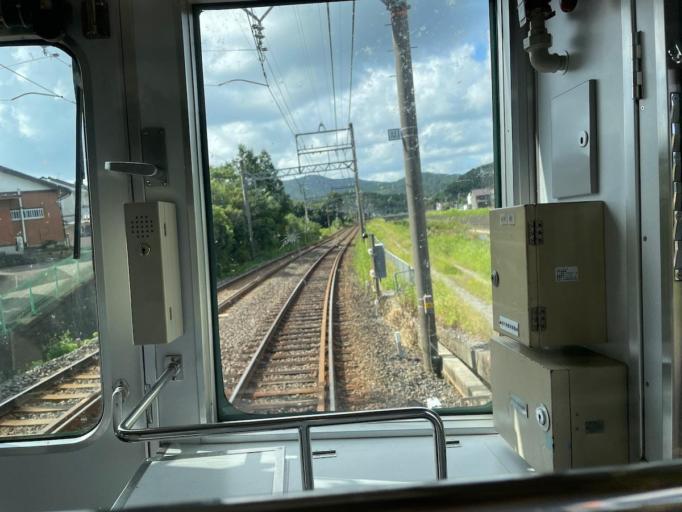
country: JP
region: Mie
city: Toba
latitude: 34.4361
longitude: 136.8431
